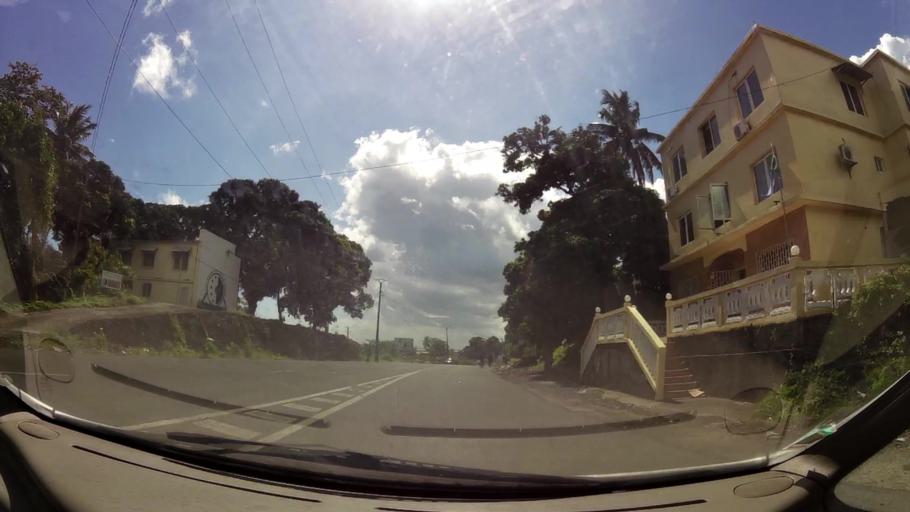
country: KM
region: Grande Comore
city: Mavingouni
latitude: -11.7127
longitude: 43.2460
